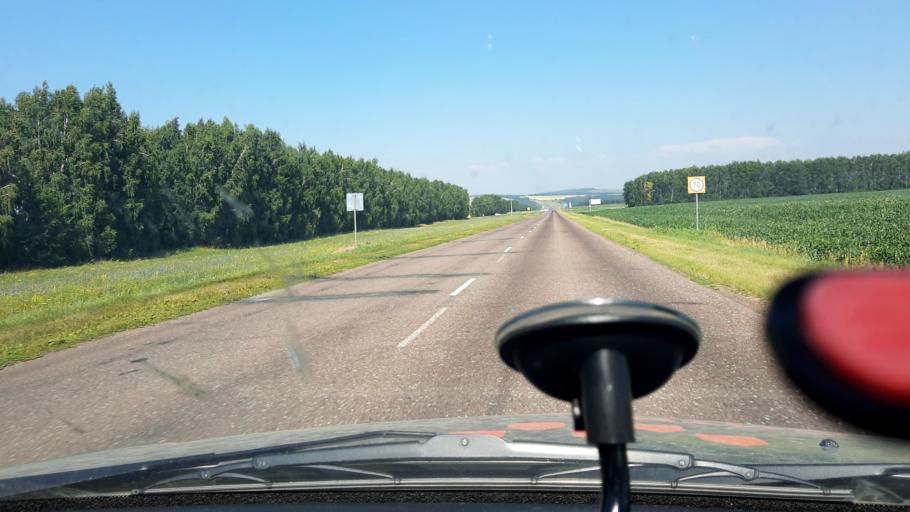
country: RU
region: Bashkortostan
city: Chekmagush
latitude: 55.1149
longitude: 54.6590
